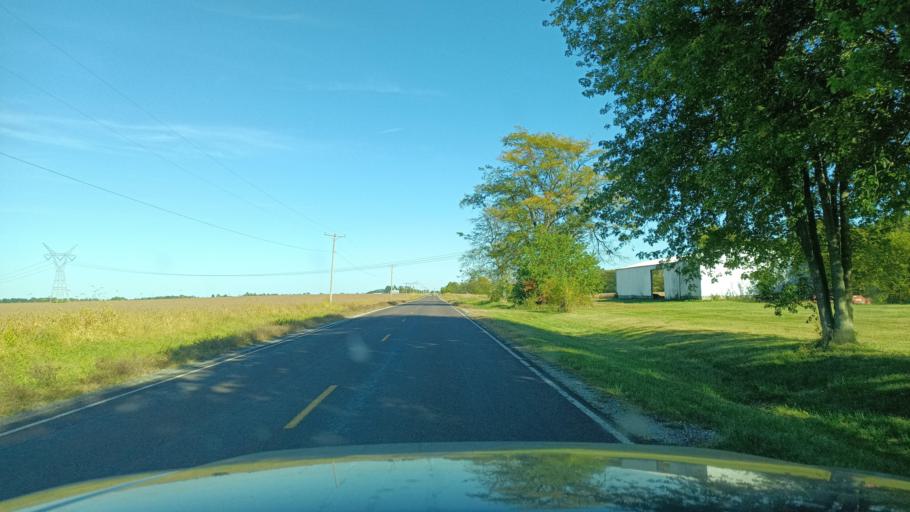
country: US
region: Illinois
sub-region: De Witt County
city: Clinton
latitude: 40.2315
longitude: -88.9938
